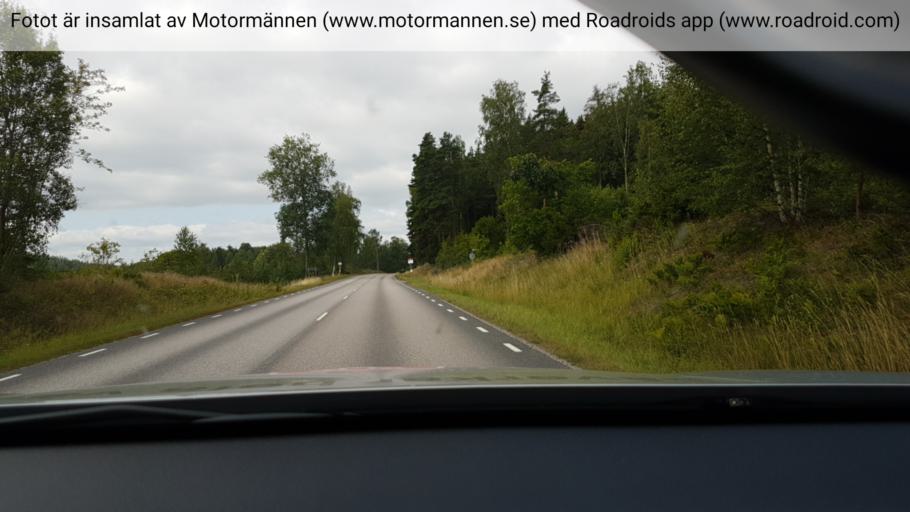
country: SE
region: Stockholm
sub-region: Norrtalje Kommun
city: Rimbo
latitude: 59.7146
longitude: 18.4434
